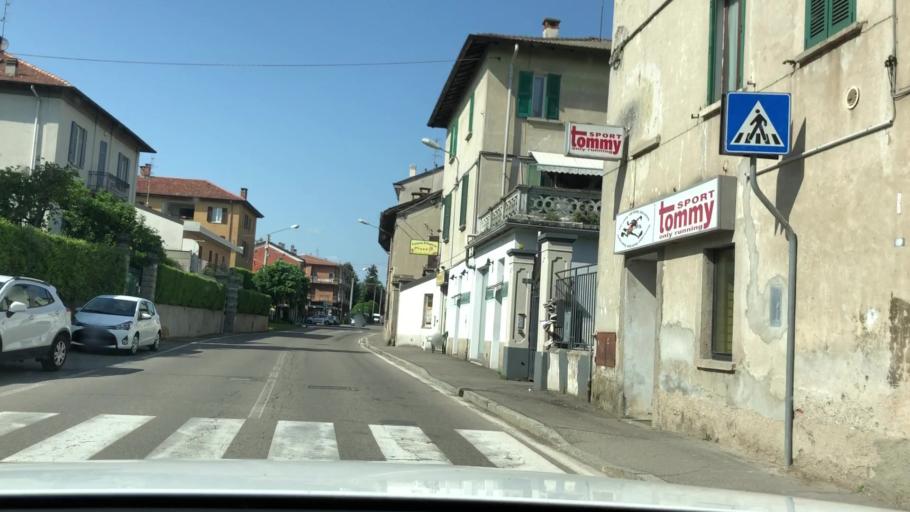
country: IT
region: Lombardy
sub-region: Provincia di Como
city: Lomazzo
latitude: 45.7106
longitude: 9.0393
